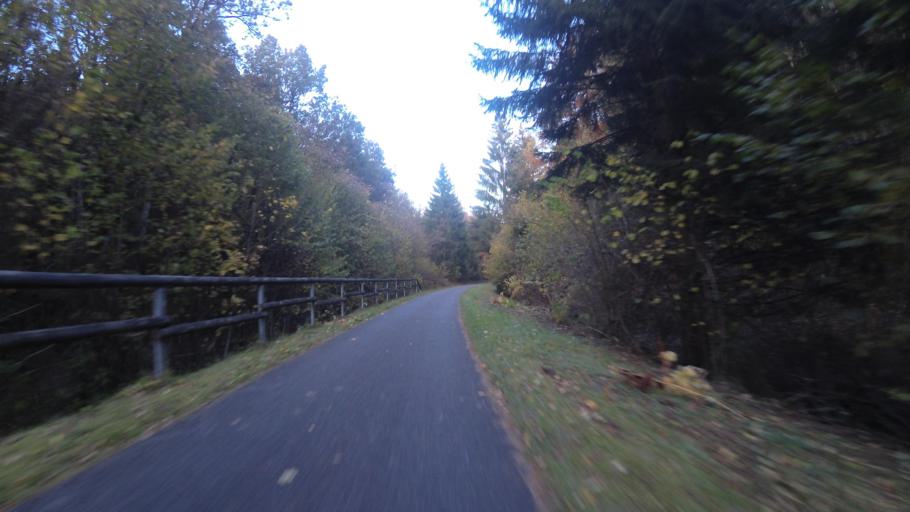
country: DE
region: Rheinland-Pfalz
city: Kell
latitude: 49.6568
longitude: 6.8487
